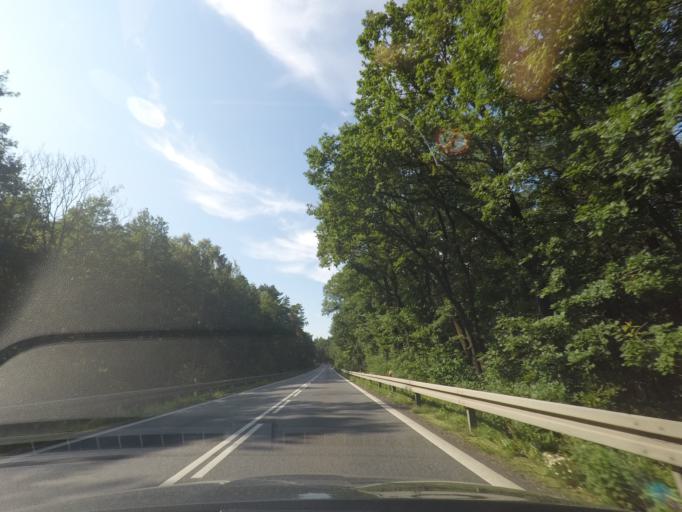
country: PL
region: Silesian Voivodeship
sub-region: Powiat pszczynski
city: Radostowice
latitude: 50.0175
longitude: 18.8493
